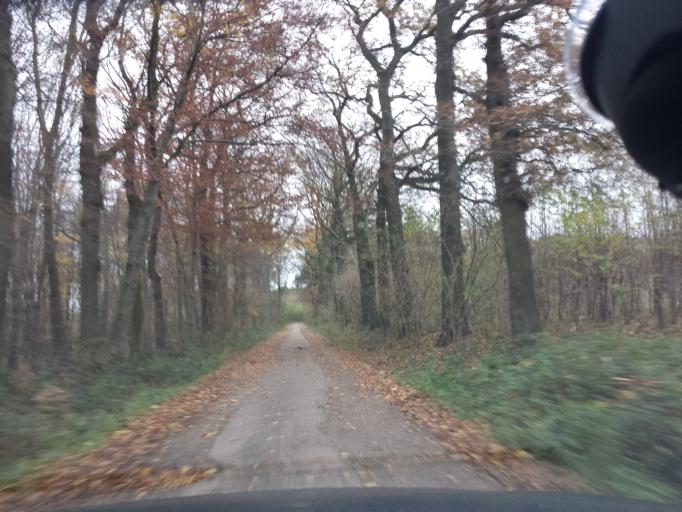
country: NL
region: Limburg
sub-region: Gemeente Heerlen
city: Heerlen
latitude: 50.9161
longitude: 6.0017
